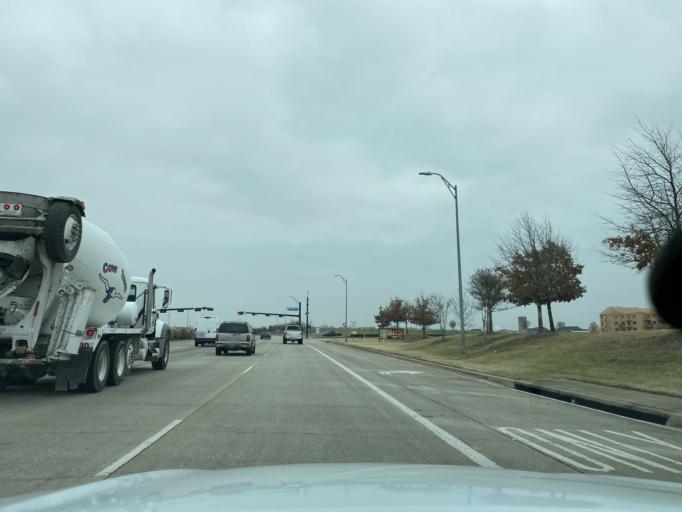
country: US
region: Texas
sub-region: Tarrant County
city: Euless
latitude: 32.7974
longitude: -97.0975
